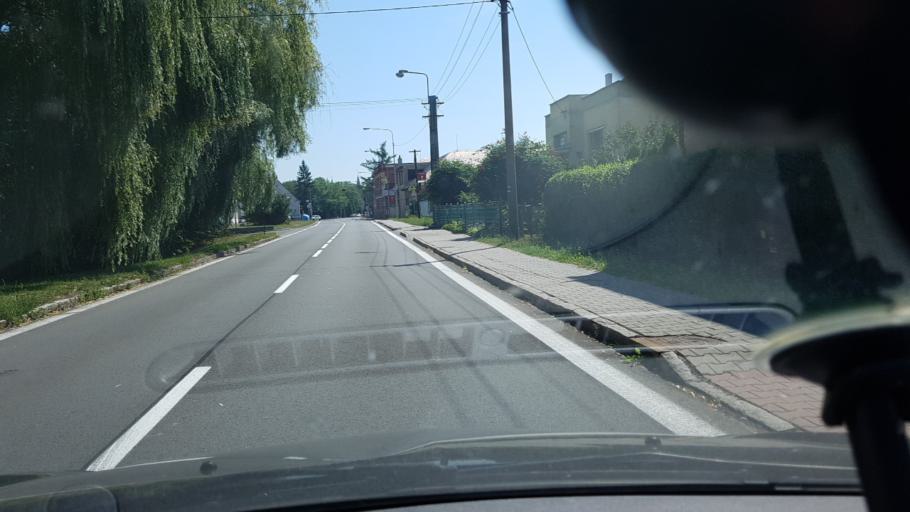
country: CZ
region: Moravskoslezsky
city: Bohumin
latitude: 49.9063
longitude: 18.3457
